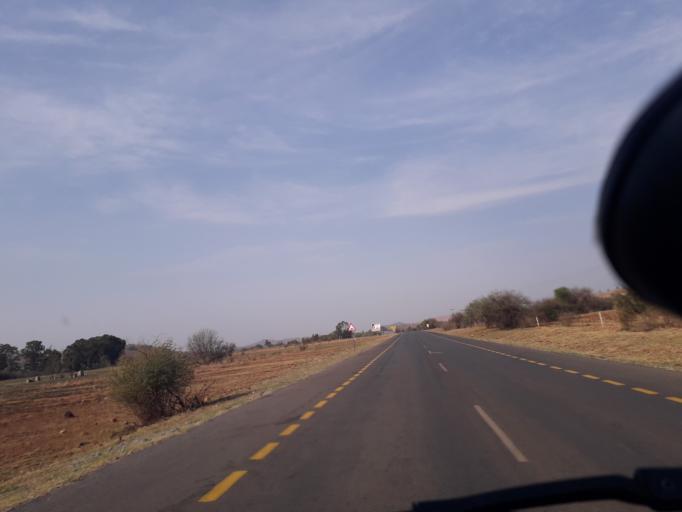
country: ZA
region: Gauteng
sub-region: West Rand District Municipality
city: Krugersdorp
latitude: -26.0131
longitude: 27.7362
